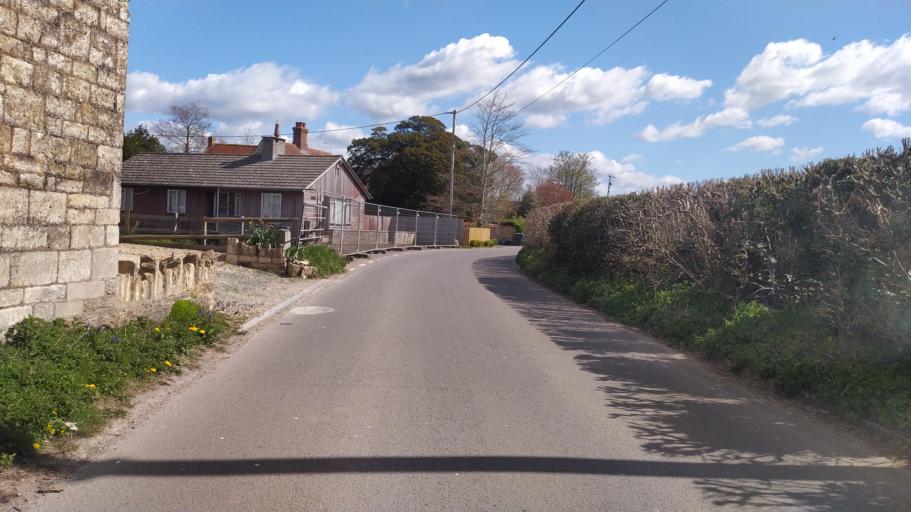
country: GB
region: England
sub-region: Dorset
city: Sturminster Newton
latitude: 50.9642
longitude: -2.3254
